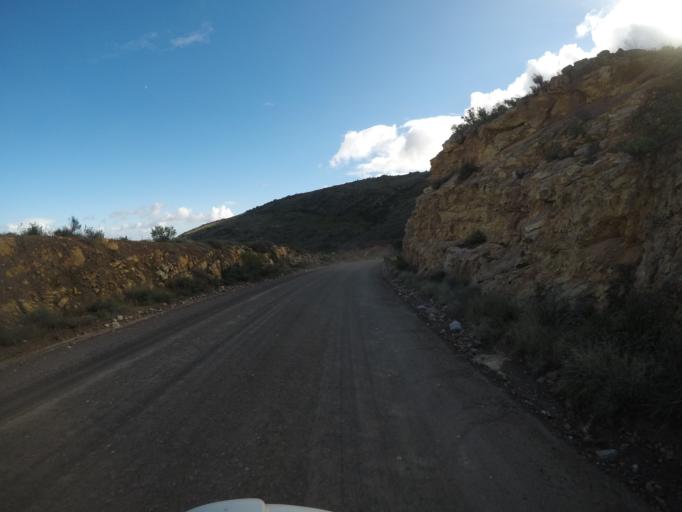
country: ZA
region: Western Cape
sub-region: West Coast District Municipality
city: Clanwilliam
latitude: -32.3487
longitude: 19.0002
